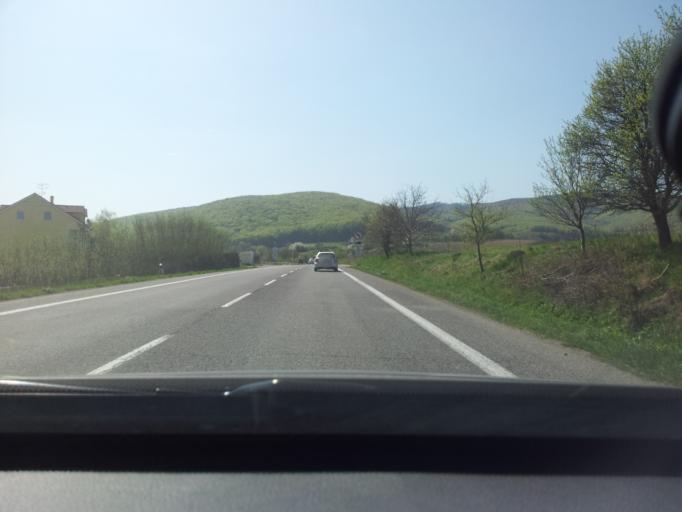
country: SK
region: Trenciansky
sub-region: Okres Trencin
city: Trencin
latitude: 48.8350
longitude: 18.0580
